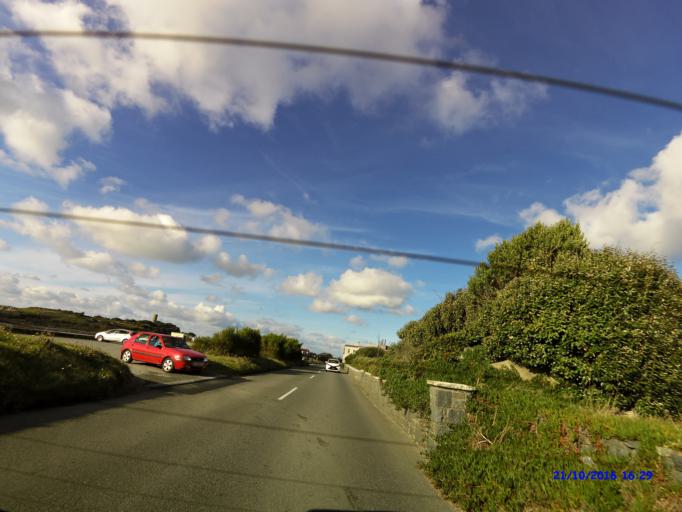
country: GG
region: St Peter Port
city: Saint Peter Port
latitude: 49.4520
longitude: -2.6501
